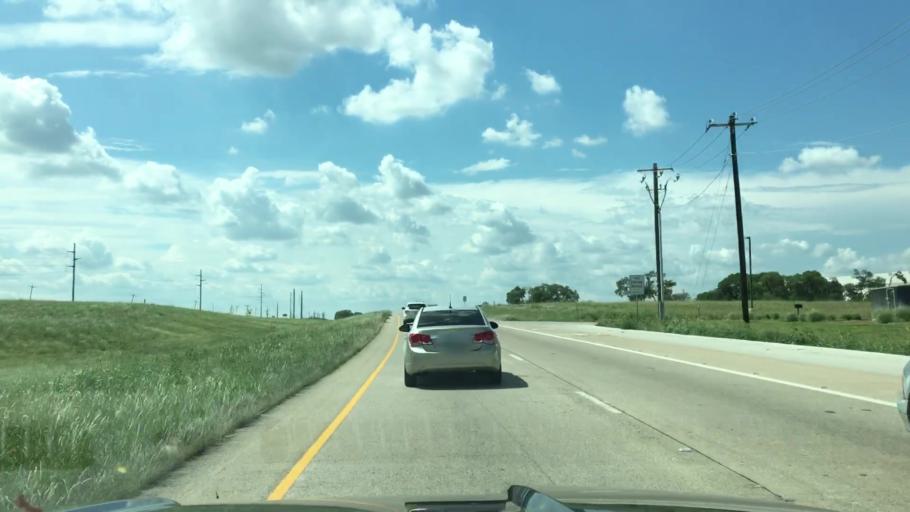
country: US
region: Texas
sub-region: Denton County
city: Roanoke
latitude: 33.0243
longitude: -97.2574
